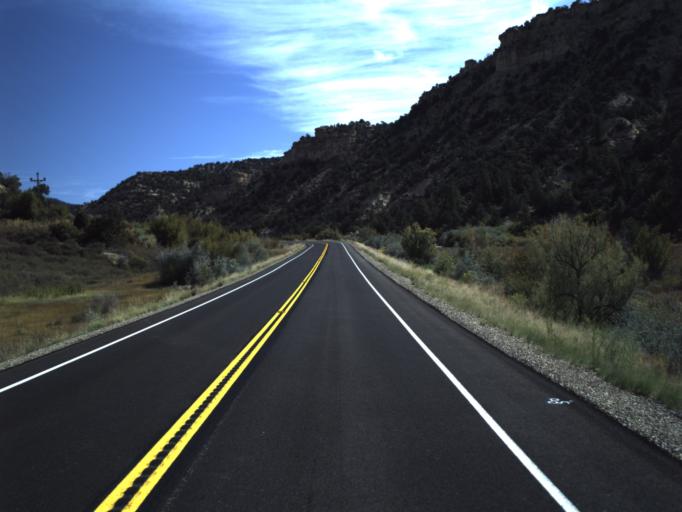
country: US
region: Utah
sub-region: Garfield County
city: Panguitch
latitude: 37.6037
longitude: -111.9139
